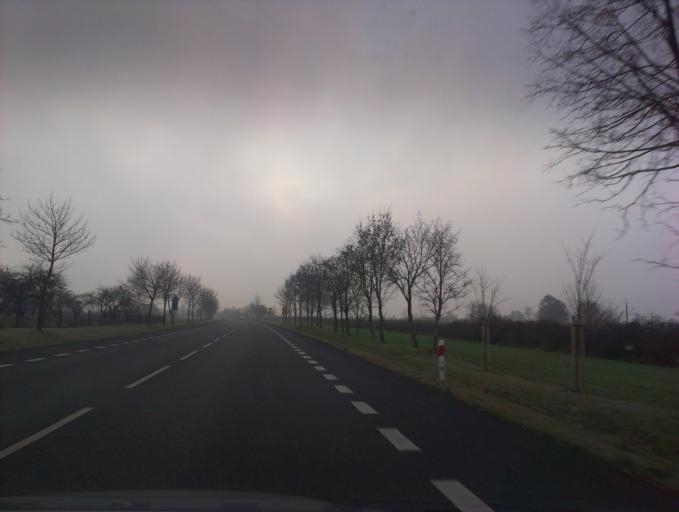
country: PL
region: Greater Poland Voivodeship
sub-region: Powiat chodzieski
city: Budzyn
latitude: 52.8875
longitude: 16.9698
